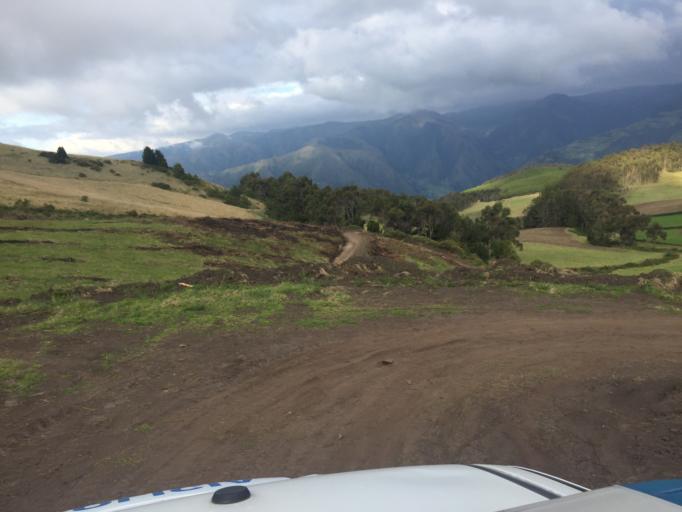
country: EC
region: Imbabura
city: Ibarra
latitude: 0.2269
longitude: -78.1219
